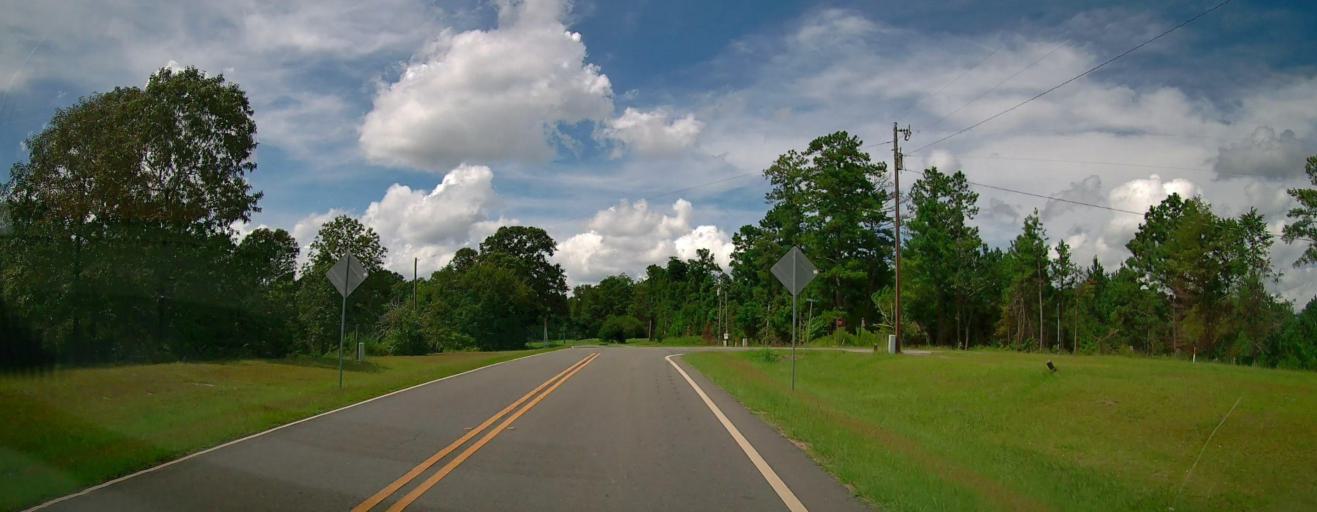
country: US
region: Georgia
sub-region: Taylor County
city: Butler
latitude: 32.5312
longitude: -84.2101
